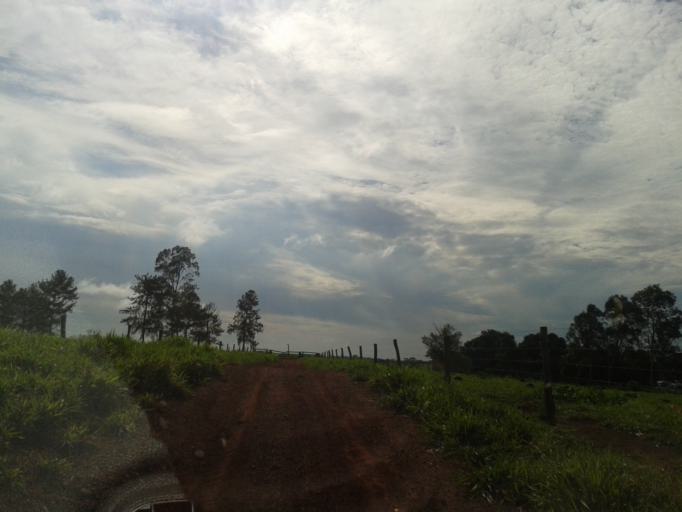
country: BR
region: Minas Gerais
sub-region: Santa Vitoria
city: Santa Vitoria
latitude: -19.2166
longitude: -50.6767
